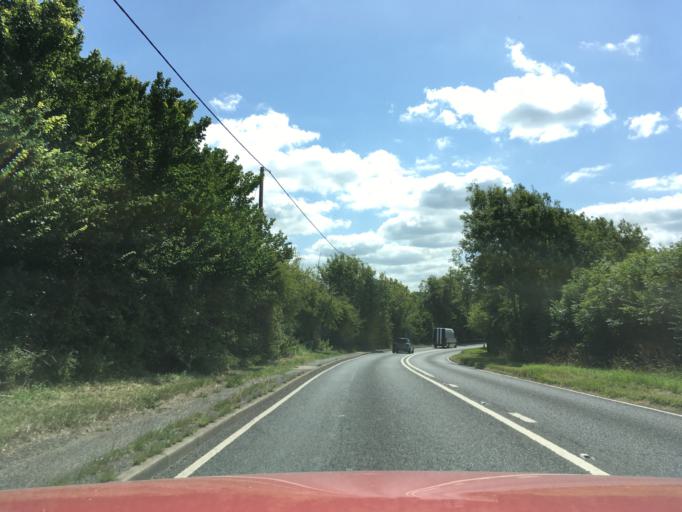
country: GB
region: England
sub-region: Buckinghamshire
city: Aylesbury
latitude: 51.8628
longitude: -0.8308
